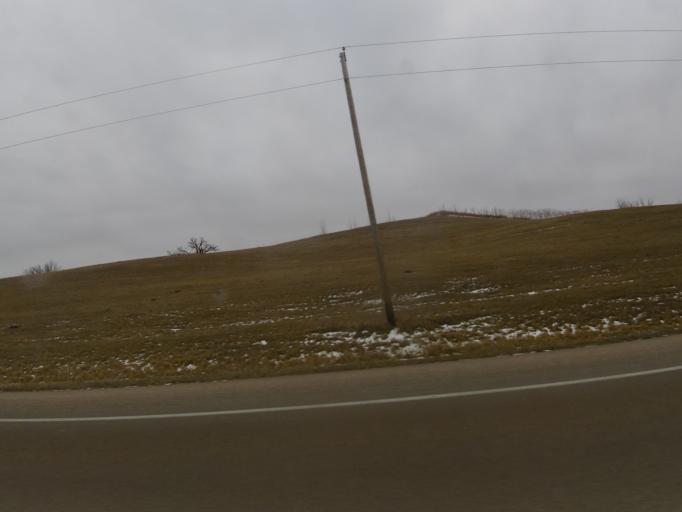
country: US
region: Minnesota
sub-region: Carver County
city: Victoria
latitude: 44.8092
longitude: -93.6607
